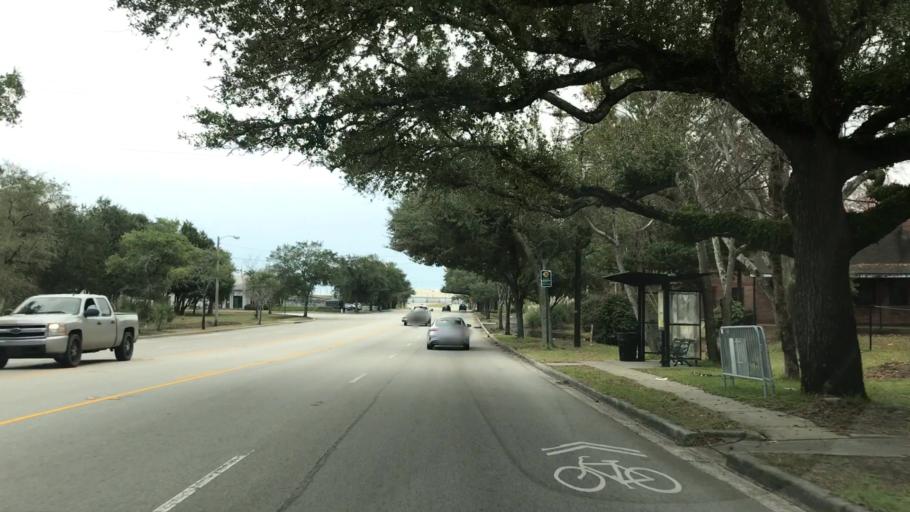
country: US
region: South Carolina
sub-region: Charleston County
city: Charleston
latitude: 32.8030
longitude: -79.9397
